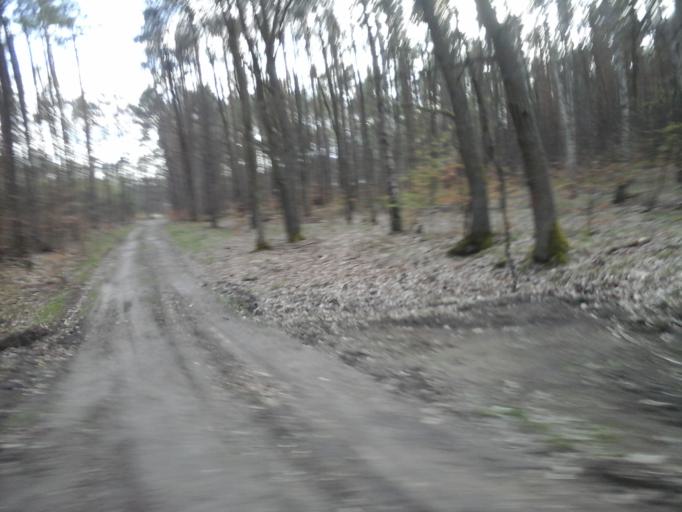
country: PL
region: West Pomeranian Voivodeship
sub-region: Powiat choszczenski
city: Bierzwnik
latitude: 53.0232
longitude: 15.5929
